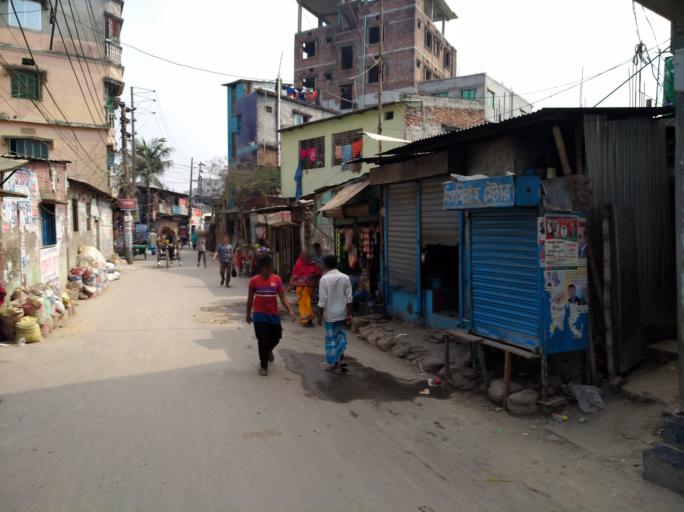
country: BD
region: Dhaka
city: Azimpur
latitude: 23.7144
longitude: 90.3777
